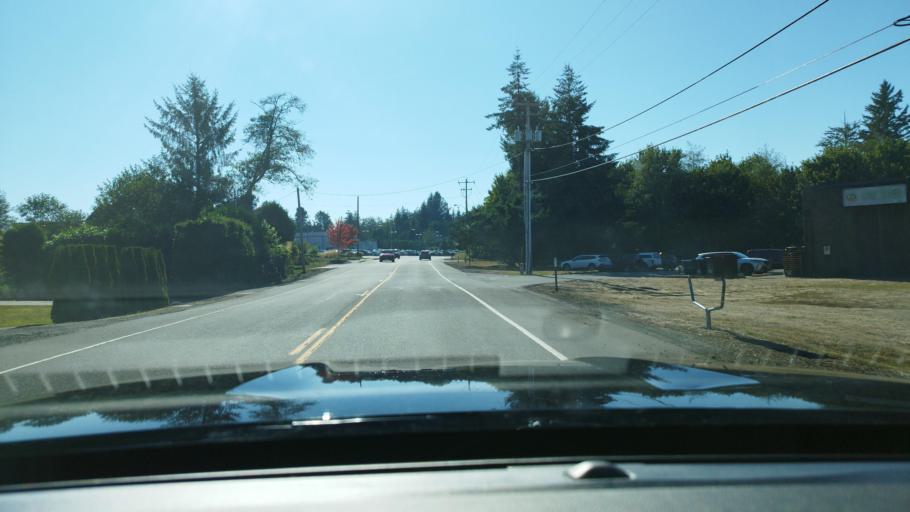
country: US
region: Oregon
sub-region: Clatsop County
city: Warrenton
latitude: 46.1508
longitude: -123.9188
